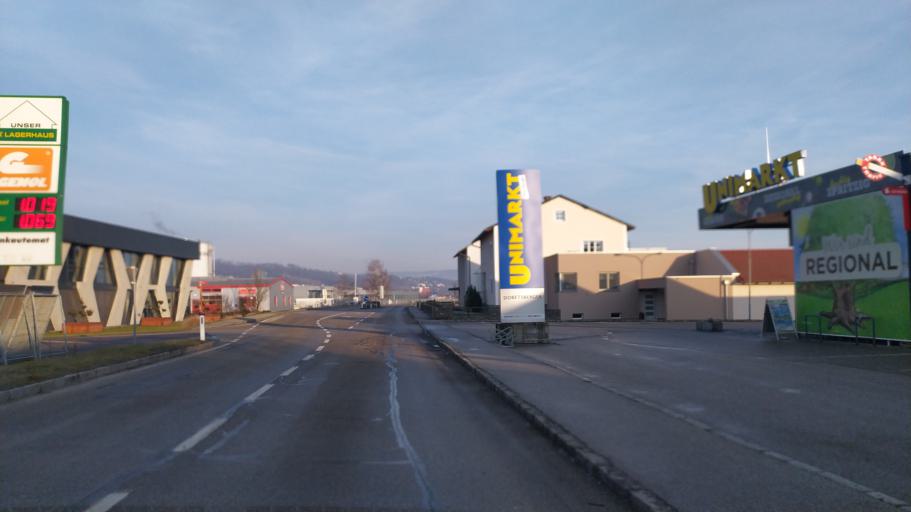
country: AT
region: Upper Austria
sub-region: Politischer Bezirk Urfahr-Umgebung
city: Feldkirchen an der Donau
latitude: 48.3465
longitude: 14.0566
